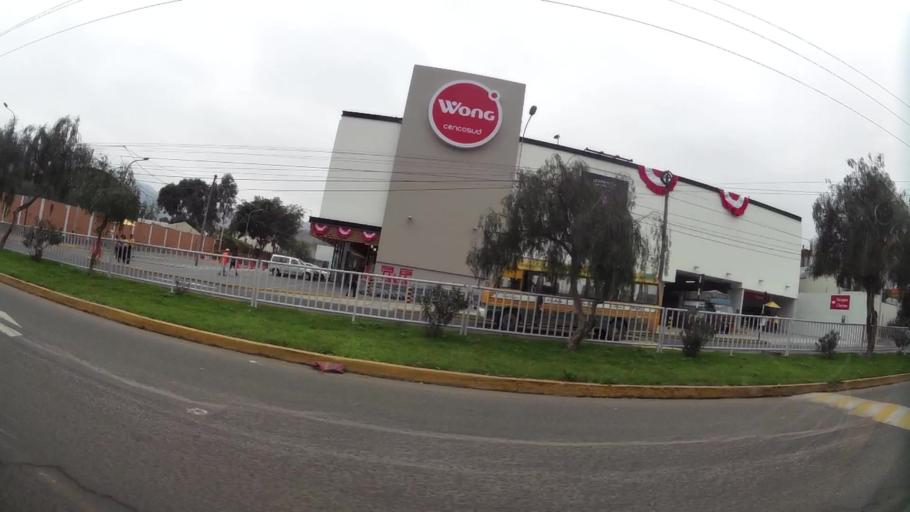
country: PE
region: Lima
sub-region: Lima
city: La Molina
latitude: -12.0861
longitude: -76.9022
